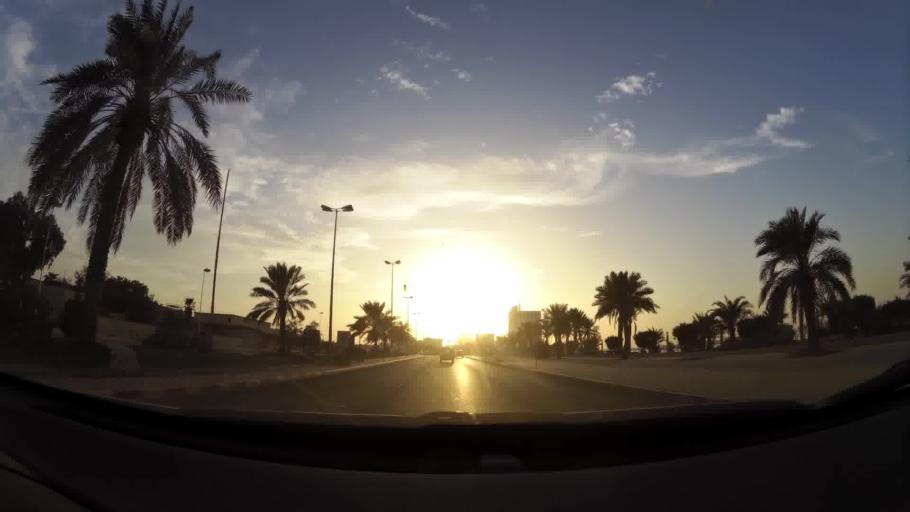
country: KW
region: Al Asimah
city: Ash Shamiyah
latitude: 29.3573
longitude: 47.9509
